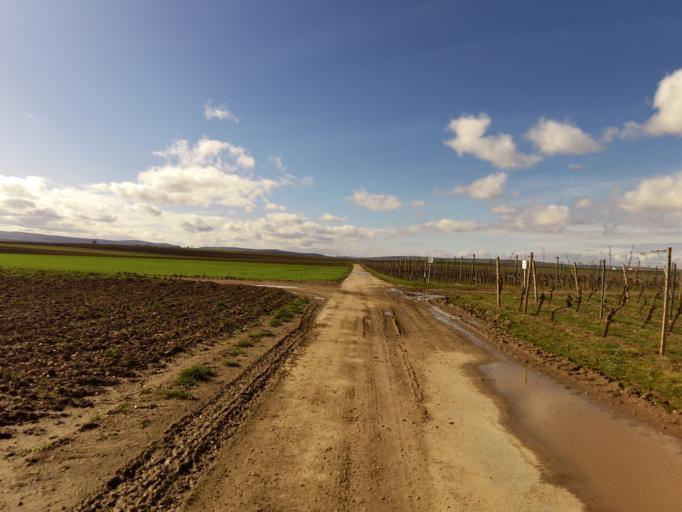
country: DE
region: Rheinland-Pfalz
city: Offstein
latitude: 49.5903
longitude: 8.2600
